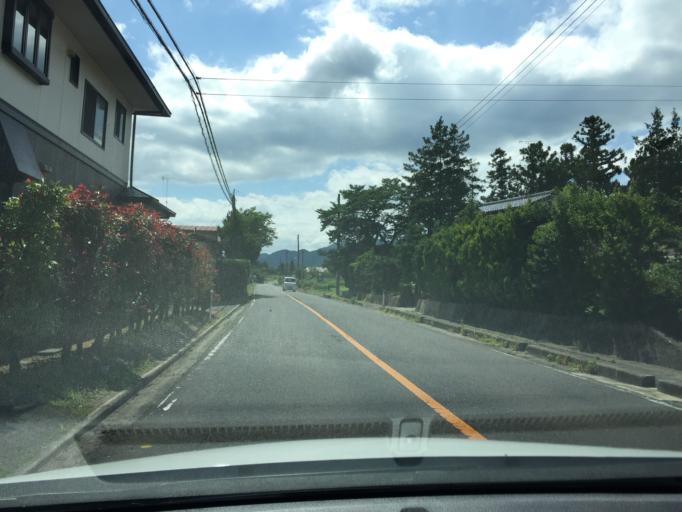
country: JP
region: Fukushima
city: Koriyama
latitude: 37.3478
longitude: 140.2717
